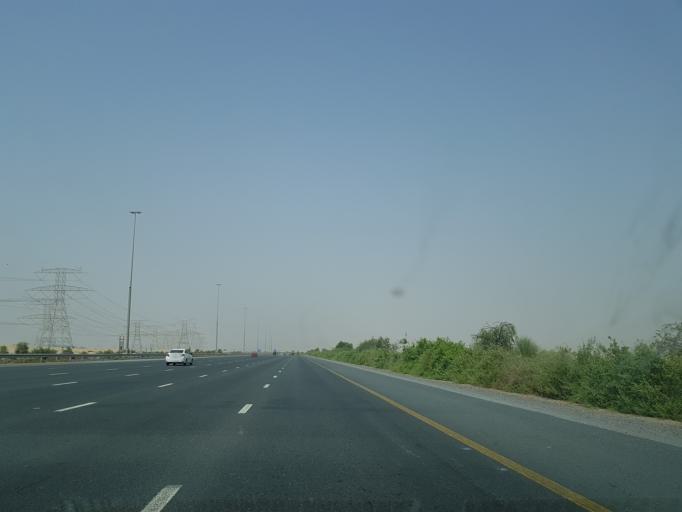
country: AE
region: Dubai
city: Dubai
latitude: 25.0663
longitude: 55.3436
